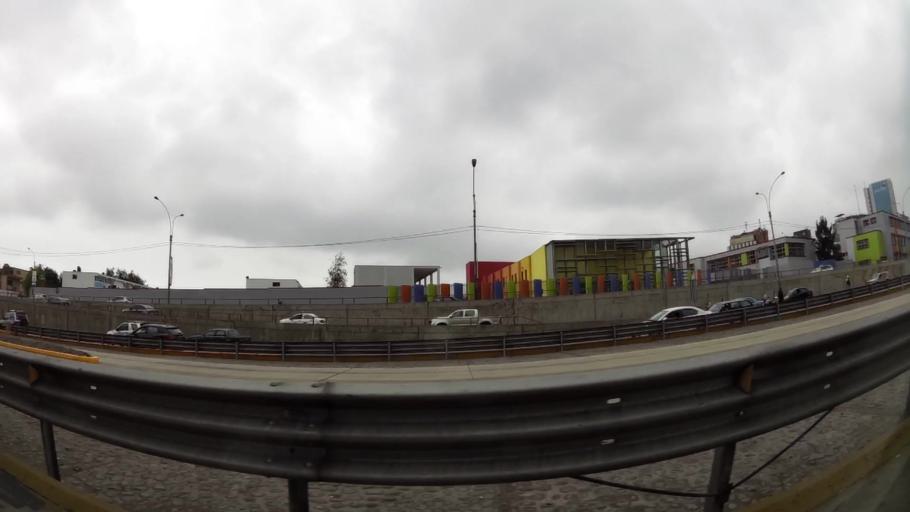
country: PE
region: Lima
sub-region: Lima
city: San Isidro
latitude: -12.1002
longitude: -77.0265
